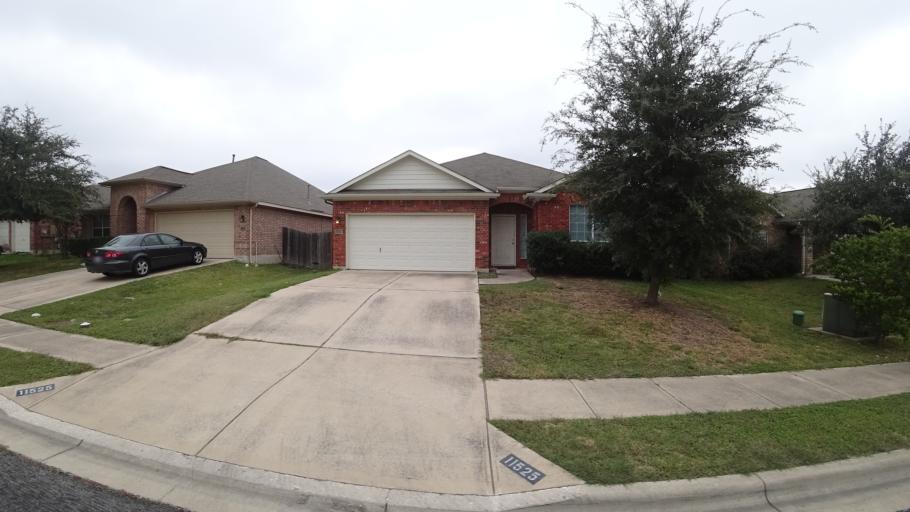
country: US
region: Texas
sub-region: Travis County
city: Pflugerville
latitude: 30.3761
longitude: -97.6532
